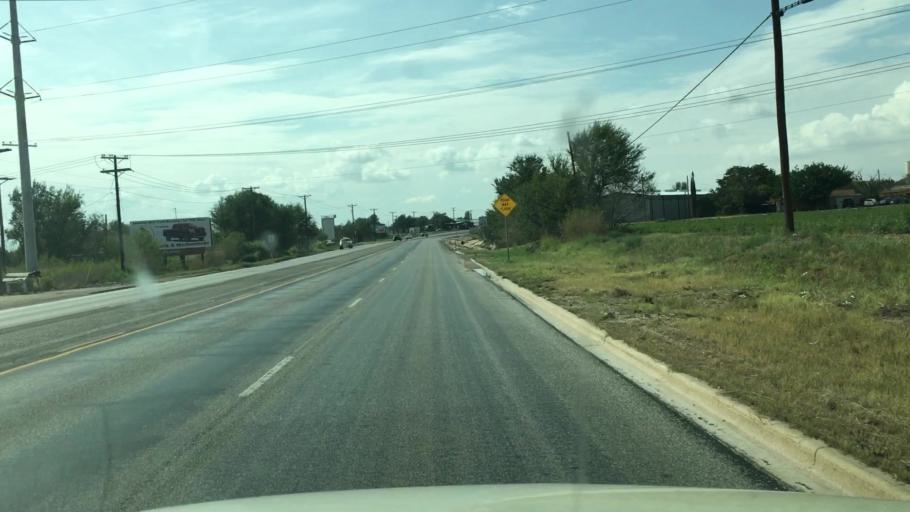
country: US
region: Texas
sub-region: Dawson County
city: Lamesa
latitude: 32.7178
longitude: -101.9421
